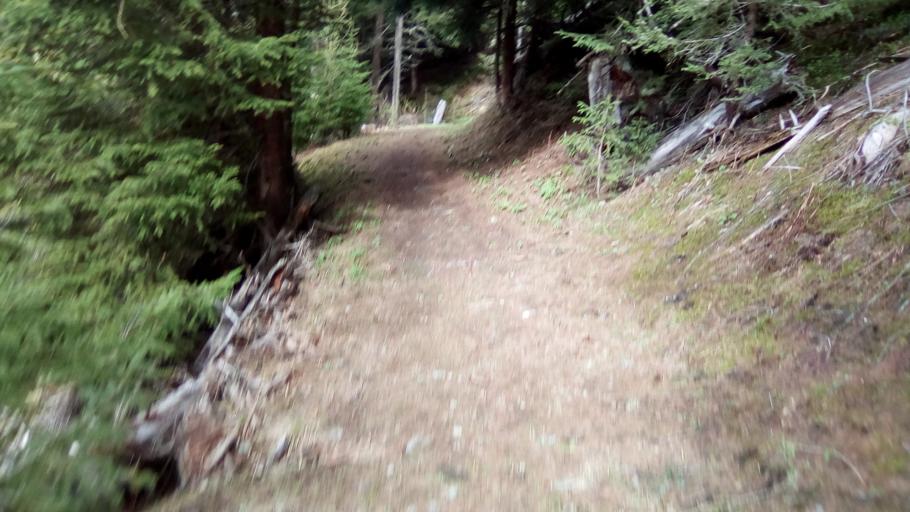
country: CH
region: Valais
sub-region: Entremont District
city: Orsieres
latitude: 46.0225
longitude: 7.1779
